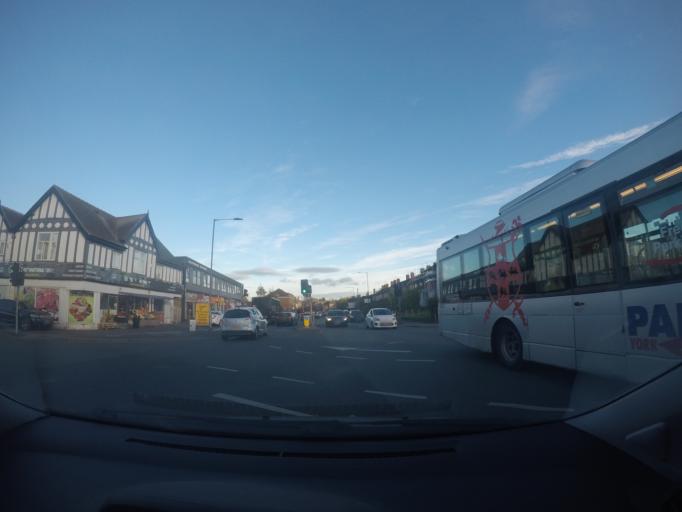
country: GB
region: England
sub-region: City of York
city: Heslington
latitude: 53.9542
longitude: -1.0592
